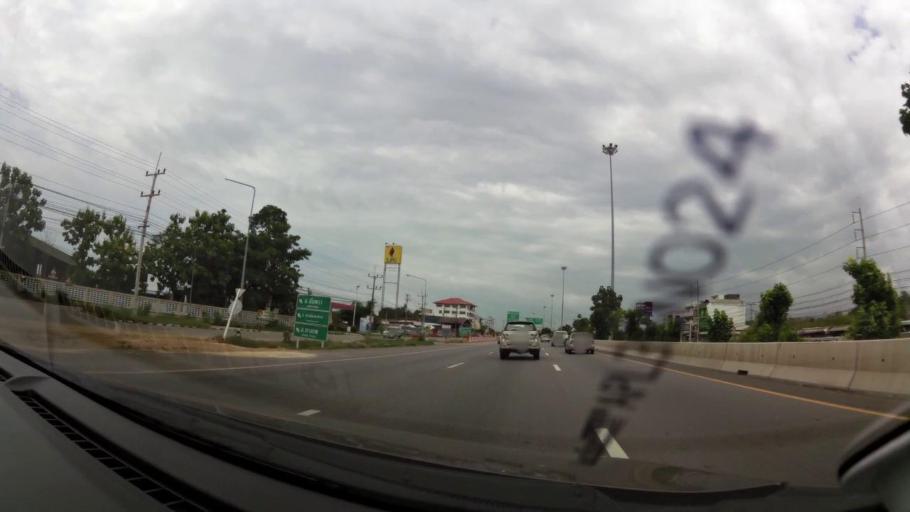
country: TH
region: Samut Songkhram
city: Samut Songkhram
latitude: 13.4035
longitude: 100.0111
